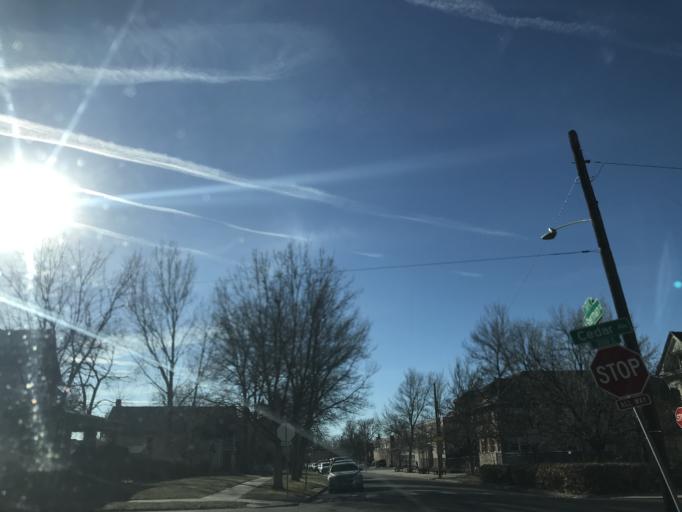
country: US
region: Colorado
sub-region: Denver County
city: Denver
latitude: 39.7131
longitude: -104.9851
